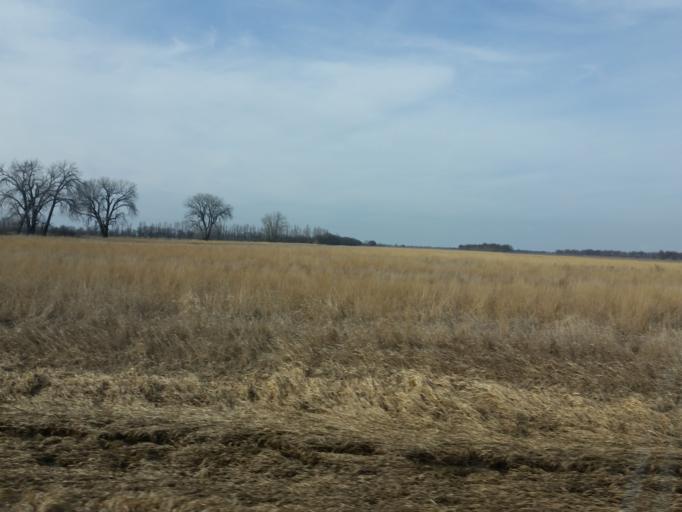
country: US
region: North Dakota
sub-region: Richland County
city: Wahpeton
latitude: 46.4711
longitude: -96.5809
